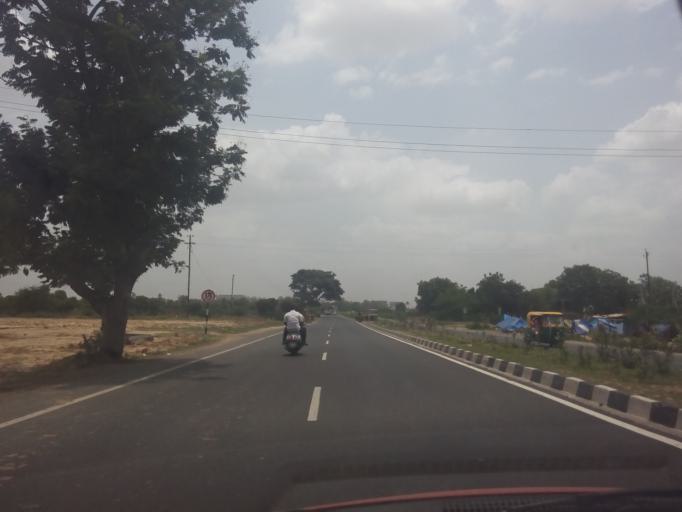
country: IN
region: Gujarat
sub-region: Ahmadabad
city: Sarkhej
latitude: 22.9866
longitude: 72.4458
